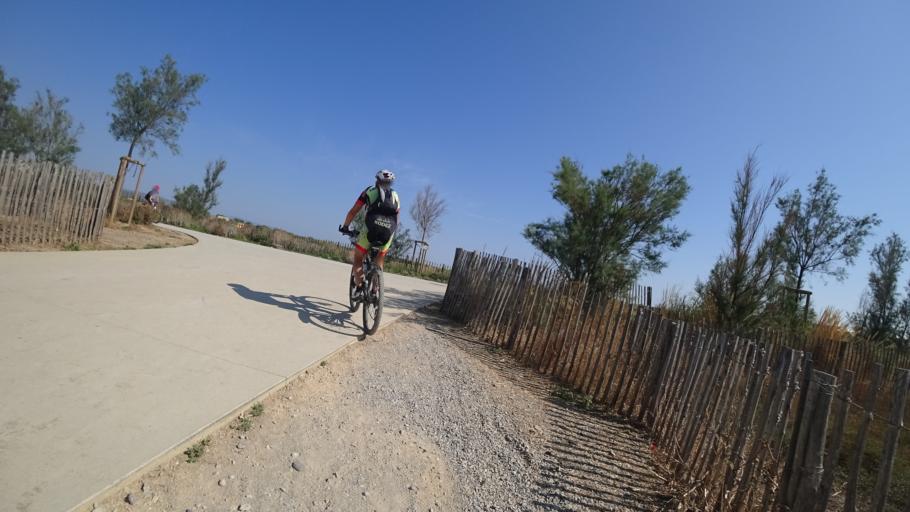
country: FR
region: Languedoc-Roussillon
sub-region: Departement des Pyrenees-Orientales
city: Le Barcares
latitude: 42.7668
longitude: 3.0372
